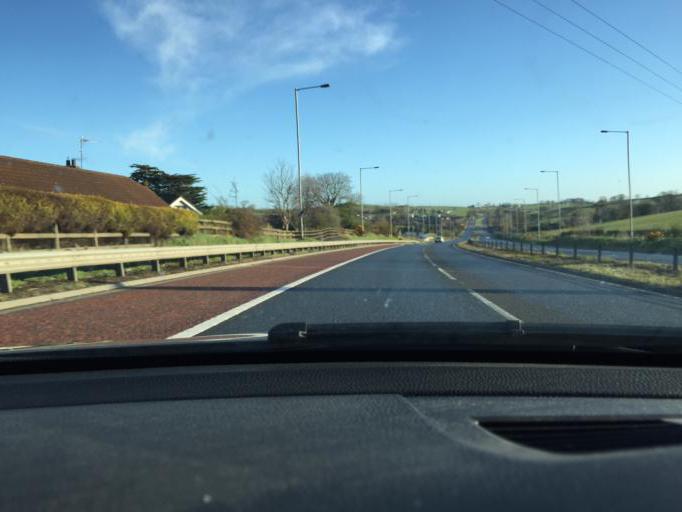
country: GB
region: Northern Ireland
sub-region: Banbridge District
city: Banbridge
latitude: 54.3175
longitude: -6.3003
